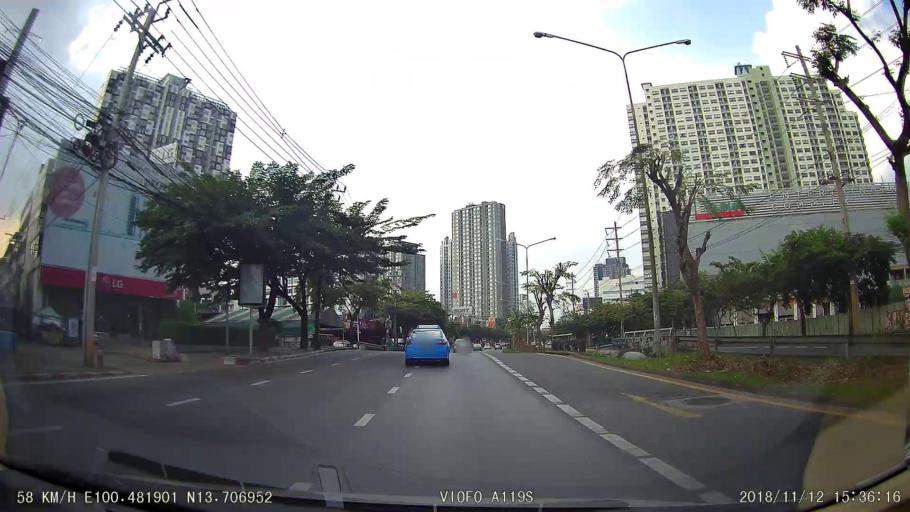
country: TH
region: Bangkok
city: Bangkok Yai
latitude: 13.7070
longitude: 100.4818
